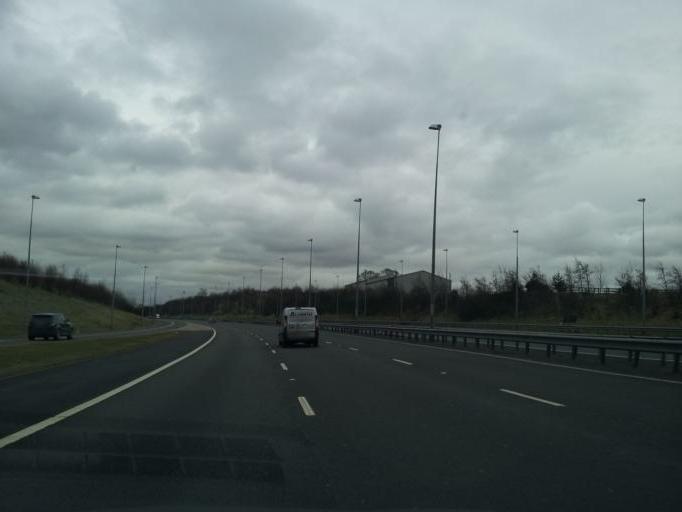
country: GB
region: England
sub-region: Staffordshire
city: Essington
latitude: 52.6648
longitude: -2.0584
